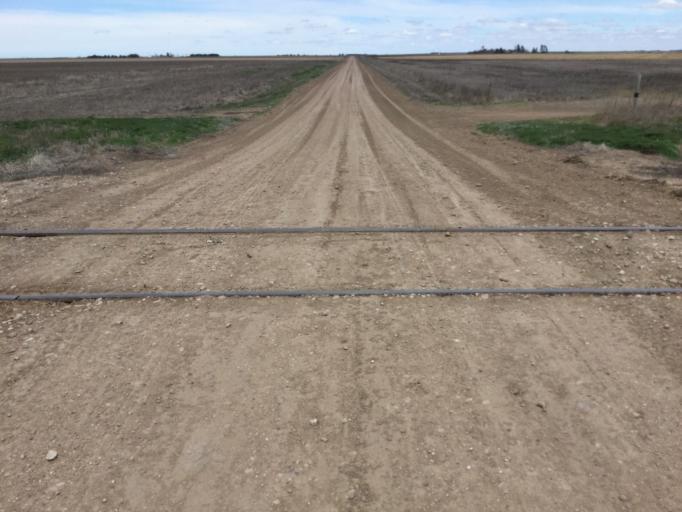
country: US
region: Kansas
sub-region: Sherman County
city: Goodland
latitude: 39.3402
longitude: -101.6701
